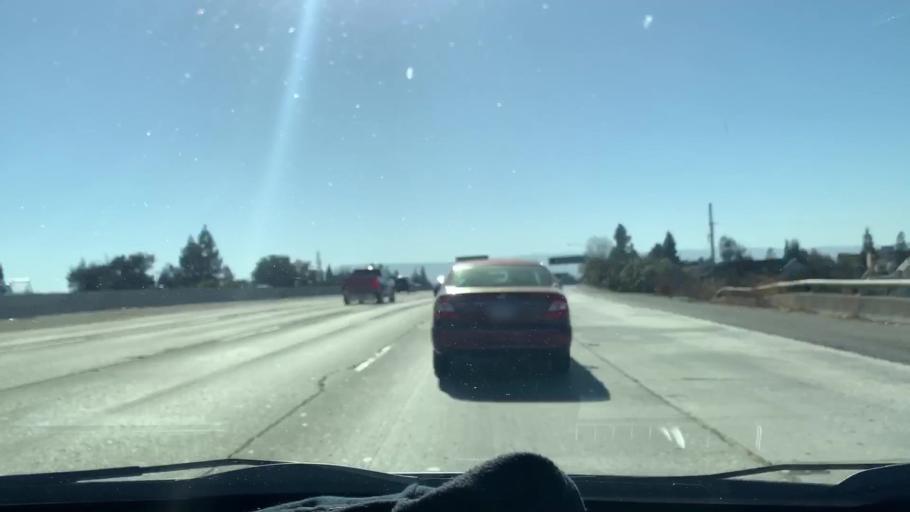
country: US
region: California
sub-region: Santa Clara County
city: Buena Vista
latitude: 37.3177
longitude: -121.9041
